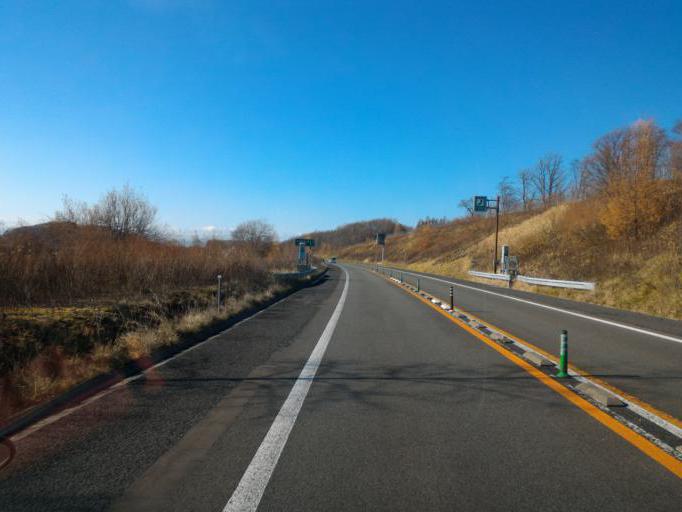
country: JP
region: Hokkaido
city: Chitose
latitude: 42.8992
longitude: 141.8488
